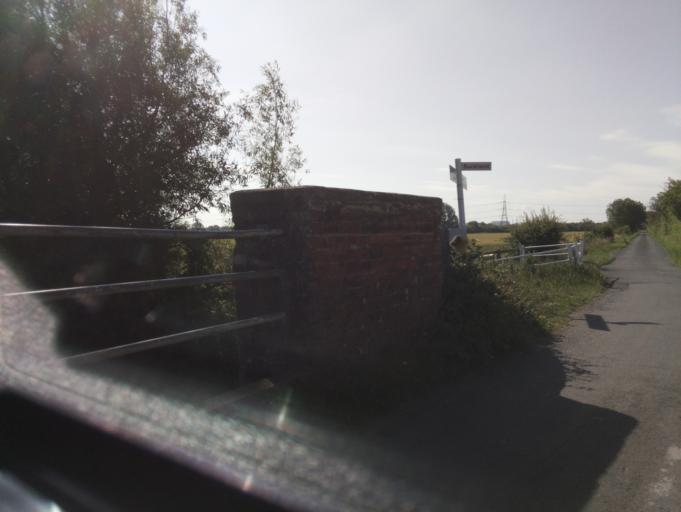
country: GB
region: England
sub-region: Oxfordshire
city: Bampton
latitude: 51.7131
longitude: -1.4926
